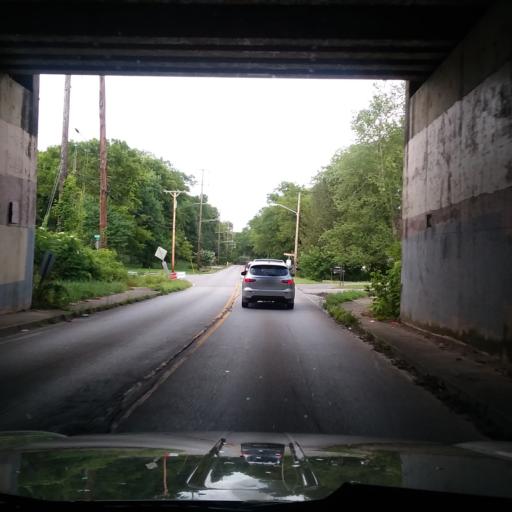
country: US
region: Tennessee
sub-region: Davidson County
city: Oak Hill
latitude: 36.0659
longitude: -86.7694
